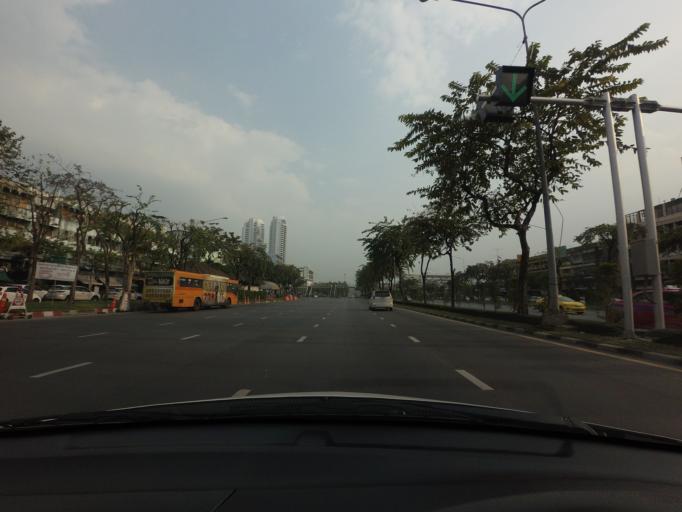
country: TH
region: Bangkok
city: Bangkok Noi
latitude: 13.7663
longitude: 100.4876
